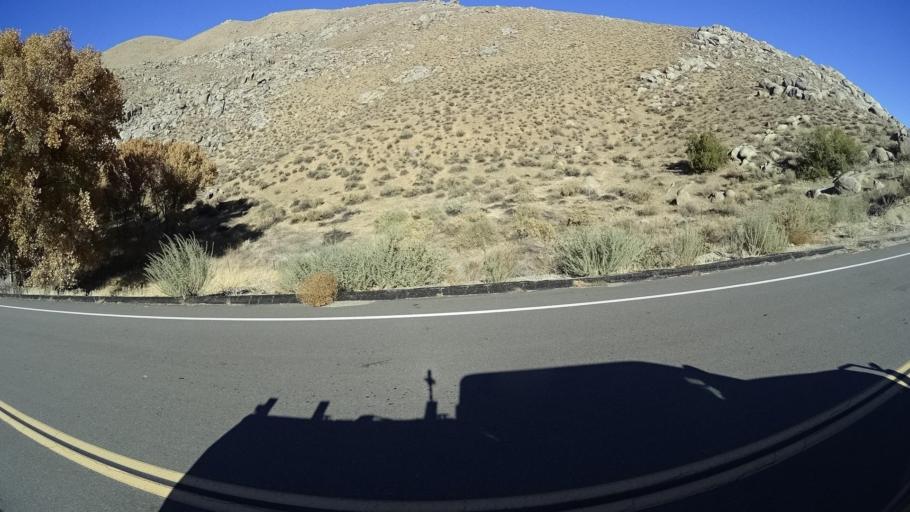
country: US
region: California
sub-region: Kern County
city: Weldon
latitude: 35.6716
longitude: -118.3383
